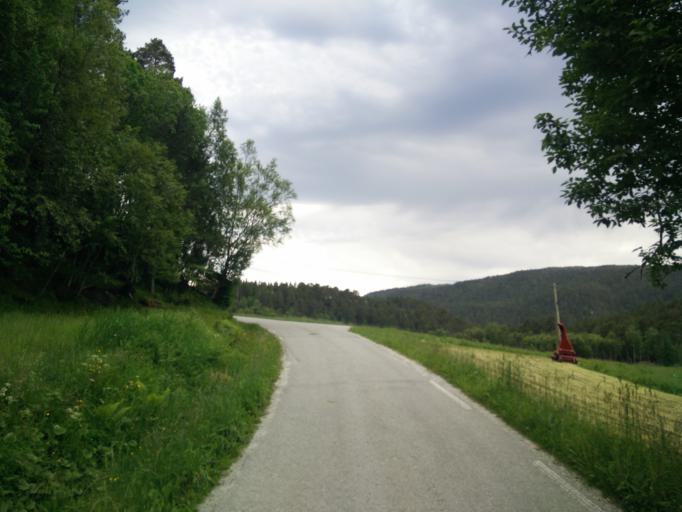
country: NO
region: More og Romsdal
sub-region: Kristiansund
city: Rensvik
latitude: 63.0386
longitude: 7.9524
